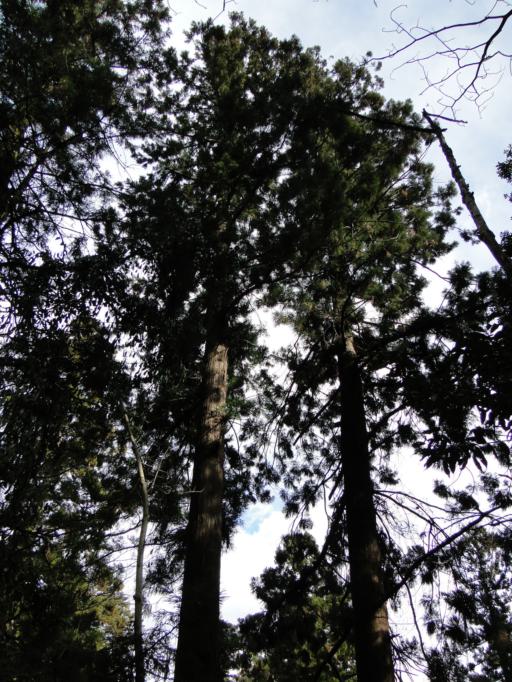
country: JP
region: Tokyo
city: Hachioji
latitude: 35.6263
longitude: 139.2522
